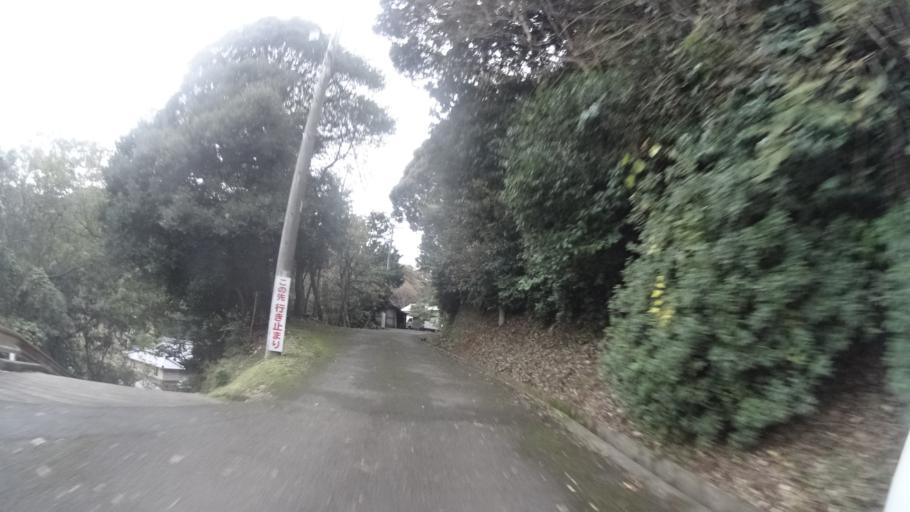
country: JP
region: Kyoto
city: Maizuru
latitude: 35.5615
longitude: 135.4675
